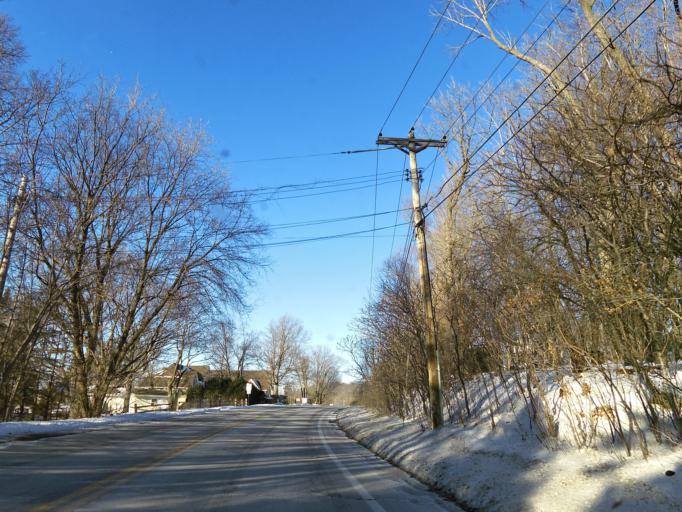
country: US
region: Minnesota
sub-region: Hennepin County
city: Mound
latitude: 44.9054
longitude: -93.6786
